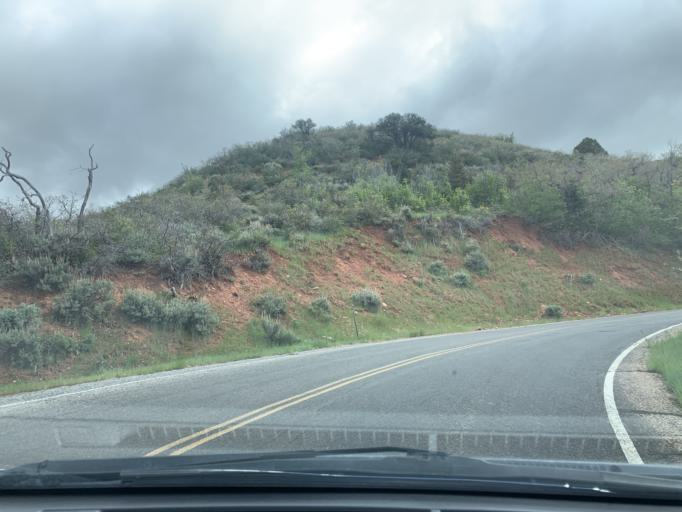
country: US
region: Utah
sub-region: Sanpete County
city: Fountain Green
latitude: 39.7900
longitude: -111.6875
